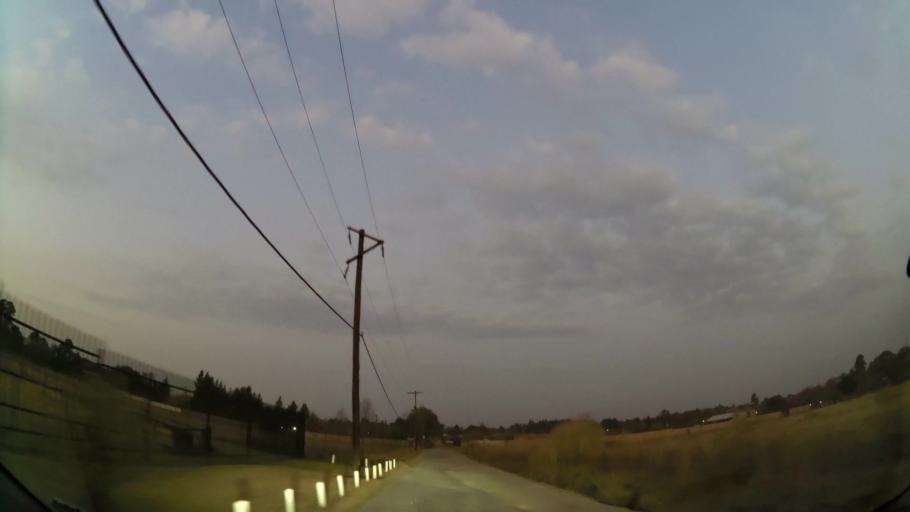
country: ZA
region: Gauteng
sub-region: Ekurhuleni Metropolitan Municipality
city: Benoni
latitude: -26.1132
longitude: 28.3060
